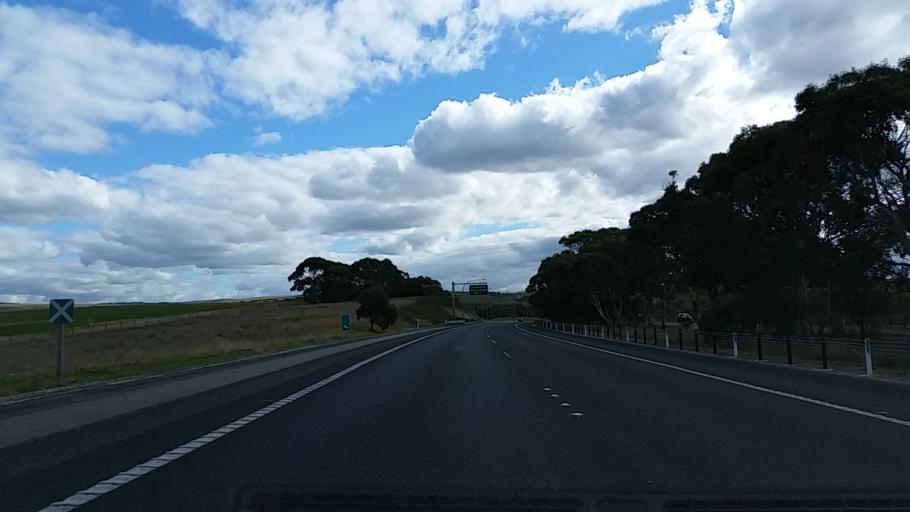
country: AU
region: South Australia
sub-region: Mount Barker
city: Callington
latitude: -35.1303
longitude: 139.0457
